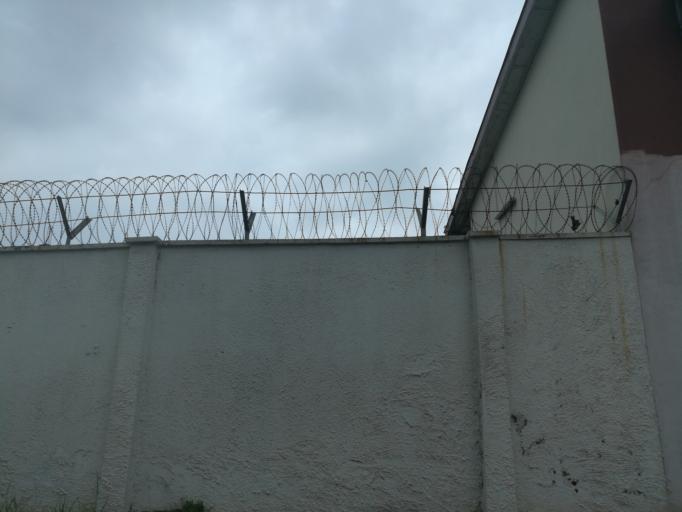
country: NG
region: Lagos
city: Lagos
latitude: 6.4468
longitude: 3.3994
